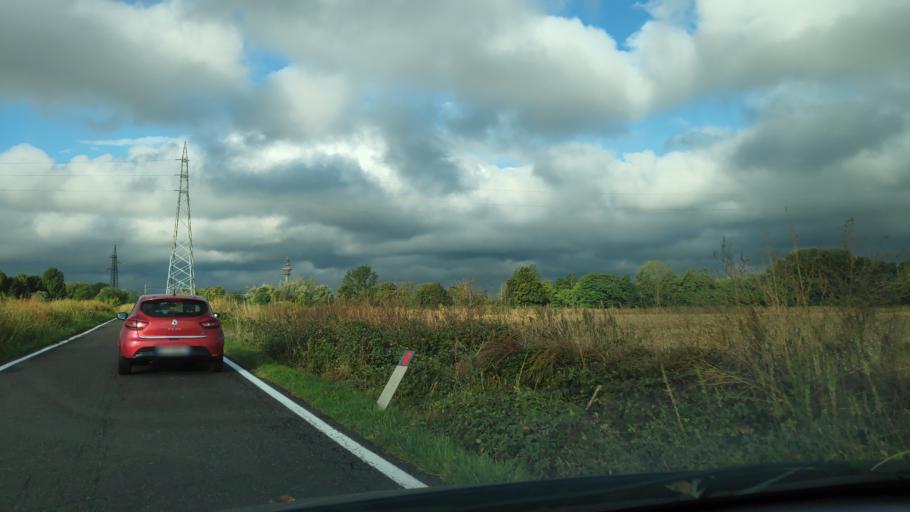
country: IT
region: Lombardy
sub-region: Citta metropolitana di Milano
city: Fizzonasco
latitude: 45.3851
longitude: 9.1937
